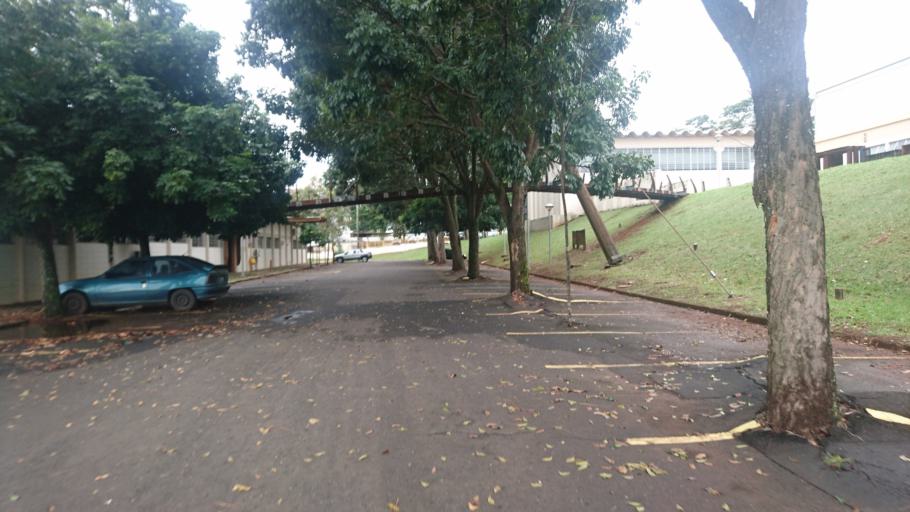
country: BR
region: Sao Paulo
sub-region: Sao Carlos
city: Sao Carlos
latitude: -22.0036
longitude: -47.8997
